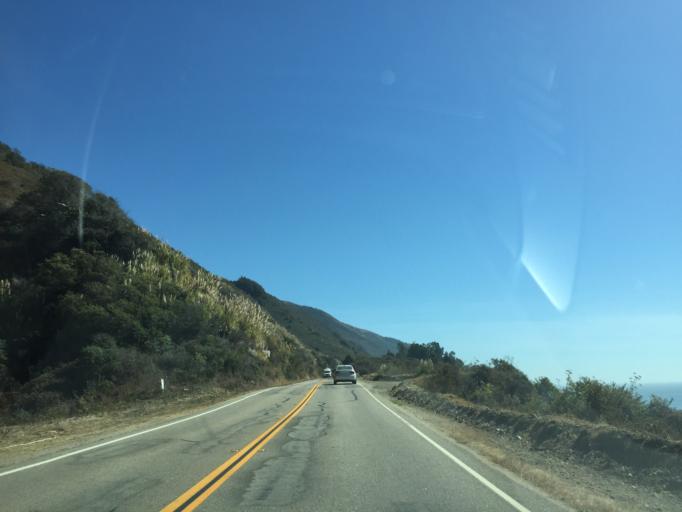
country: US
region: California
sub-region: Monterey County
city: Greenfield
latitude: 35.9992
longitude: -121.5005
